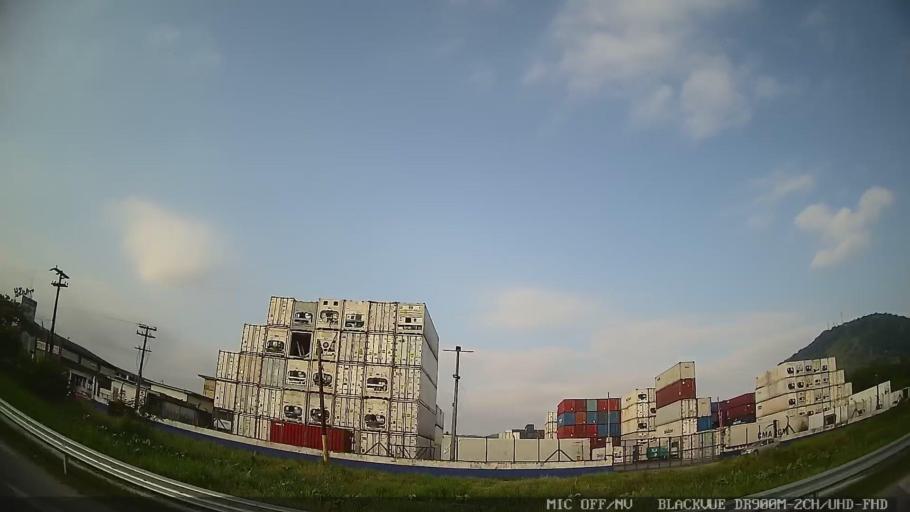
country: BR
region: Sao Paulo
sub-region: Guaruja
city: Guaruja
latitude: -23.9733
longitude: -46.2688
